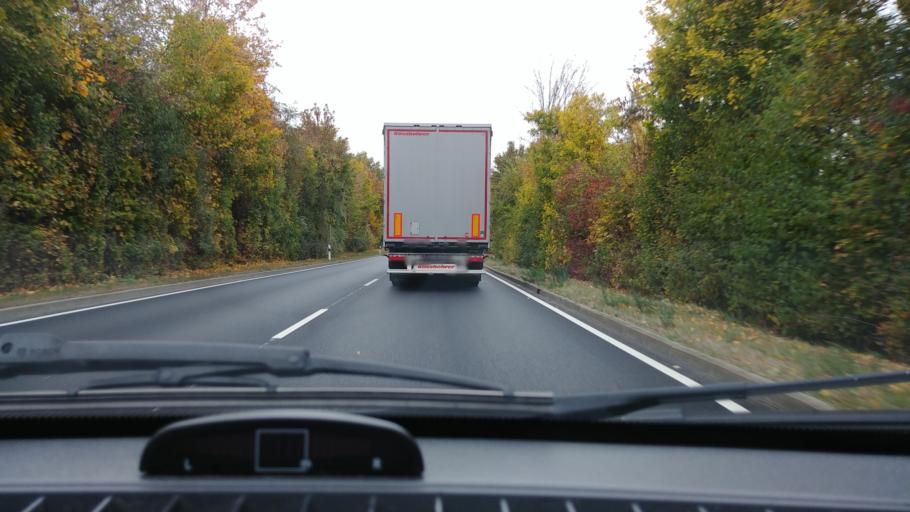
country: DE
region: Baden-Wuerttemberg
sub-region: Regierungsbezirk Stuttgart
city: Bad Mergentheim
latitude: 49.4852
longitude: 9.7665
